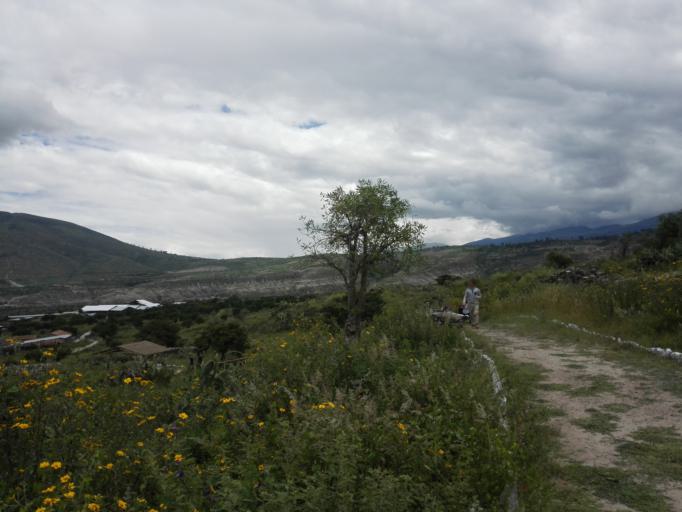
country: PE
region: Ayacucho
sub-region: Provincia de Huamanga
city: Pacaycasa
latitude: -13.0629
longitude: -74.1963
